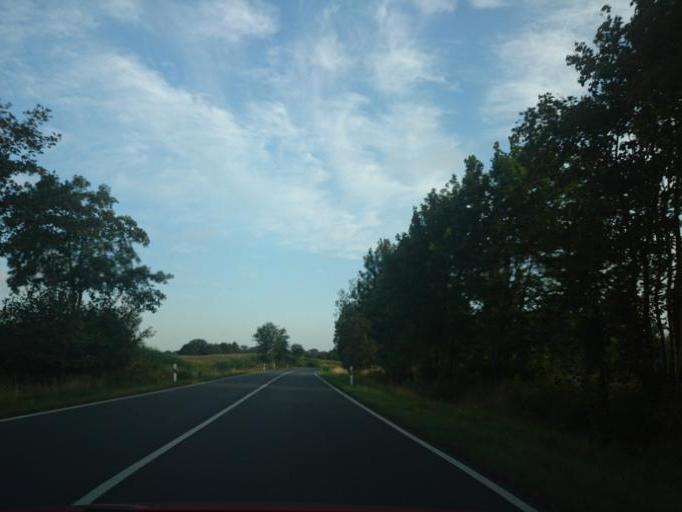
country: DE
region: Mecklenburg-Vorpommern
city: Mesekenhagen
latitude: 54.2064
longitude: 13.2532
